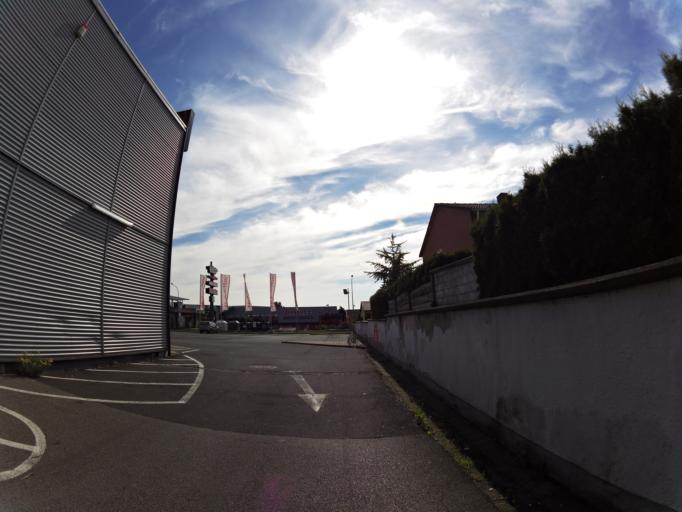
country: NL
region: Limburg
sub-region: Gemeente Kerkrade
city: Kerkrade
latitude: 50.8511
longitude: 6.0763
